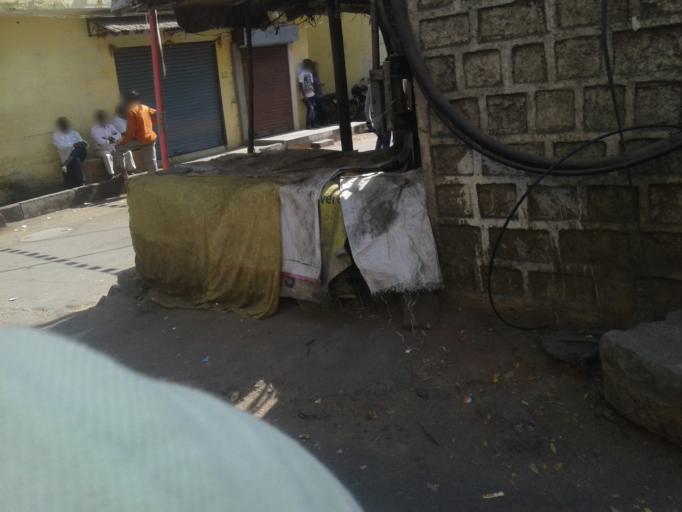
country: IN
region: Telangana
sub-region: Hyderabad
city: Hyderabad
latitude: 17.4070
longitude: 78.4822
